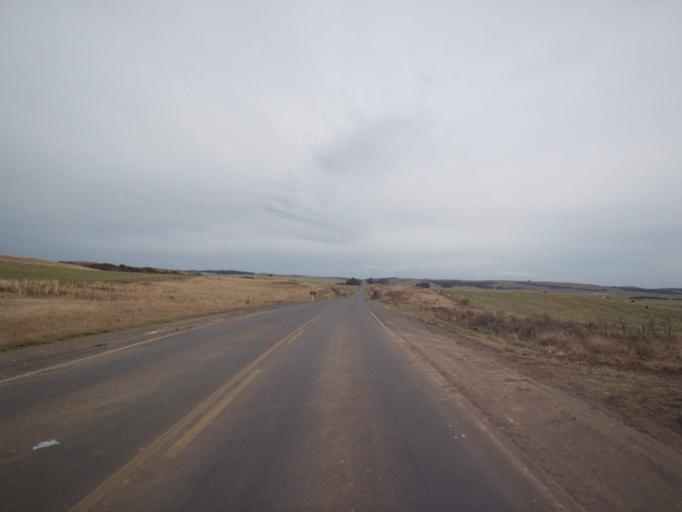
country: BR
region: Parana
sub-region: Palmas
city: Palmas
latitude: -26.7659
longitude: -51.6702
